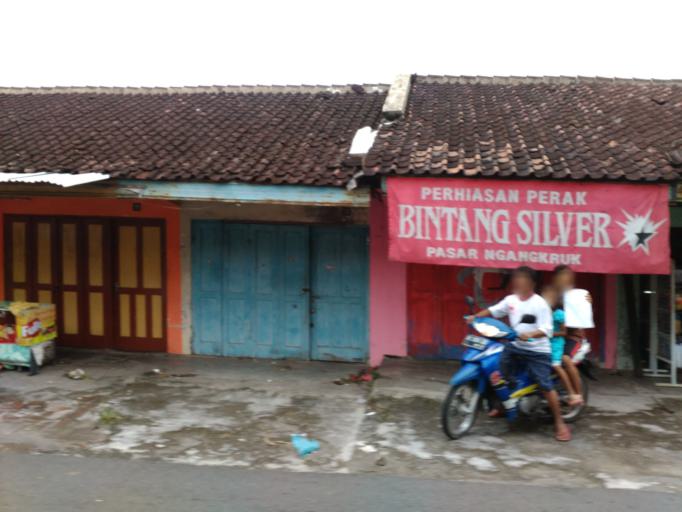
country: ID
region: Central Java
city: Boyolali
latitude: -7.5816
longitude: 110.5964
